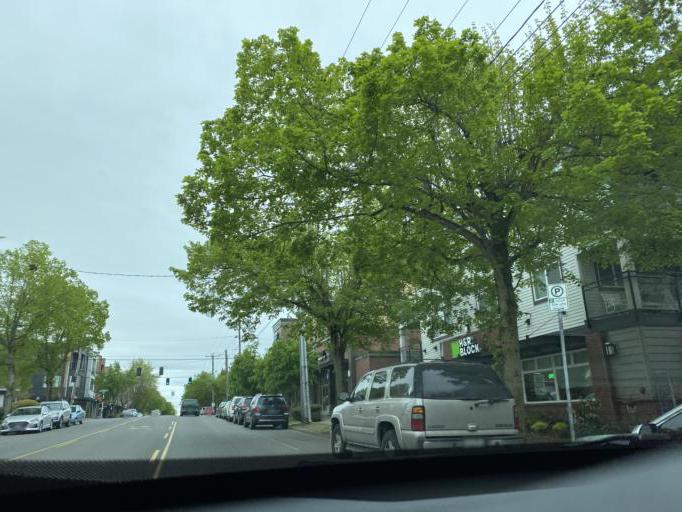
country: US
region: Washington
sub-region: King County
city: White Center
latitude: 47.5710
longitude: -122.3868
